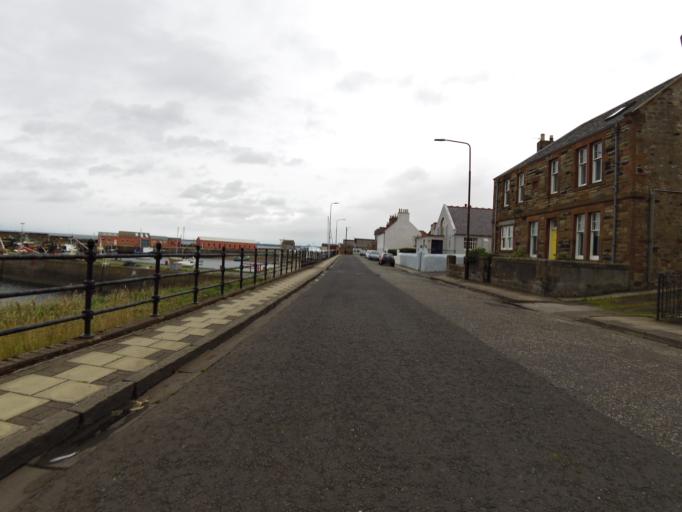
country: GB
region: Scotland
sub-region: East Lothian
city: Cockenzie
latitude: 55.9720
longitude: -2.9556
